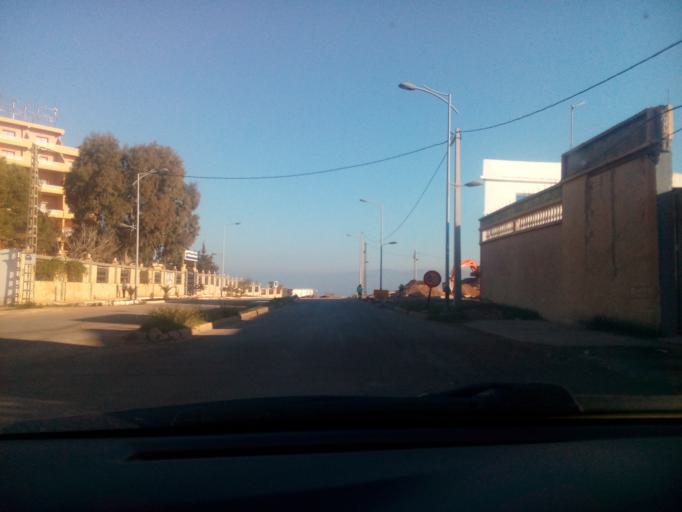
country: DZ
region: Oran
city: Bir el Djir
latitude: 35.7601
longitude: -0.5346
